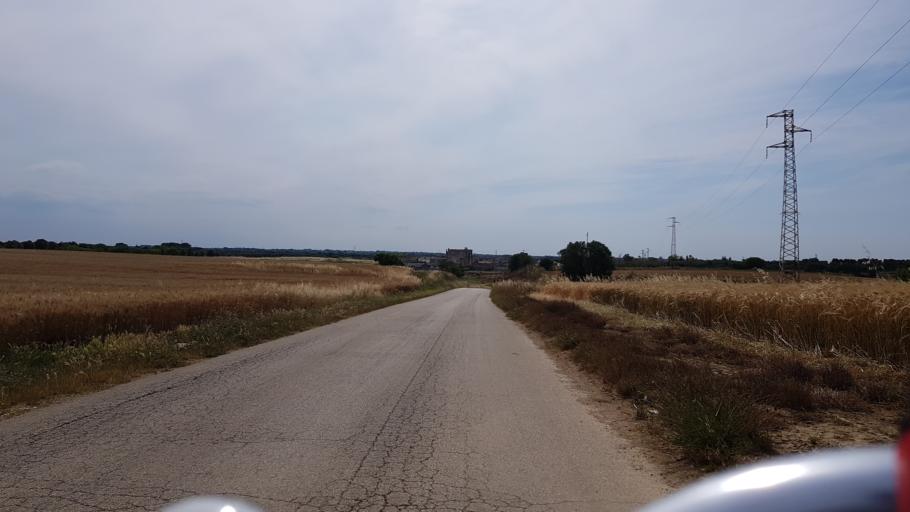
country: IT
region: Apulia
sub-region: Provincia di Brindisi
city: San Vito dei Normanni
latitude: 40.6648
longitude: 17.8000
